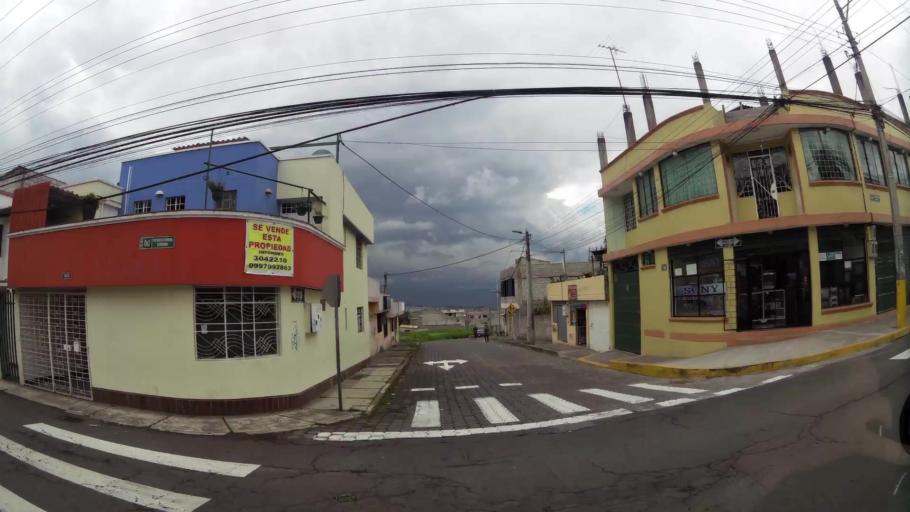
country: EC
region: Pichincha
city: Sangolqui
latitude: -0.3465
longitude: -78.5546
